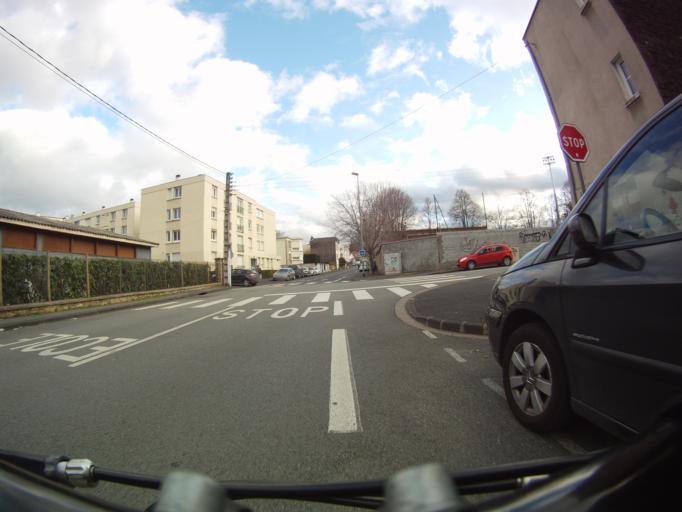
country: FR
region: Auvergne
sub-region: Departement du Puy-de-Dome
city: Beaumont
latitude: 45.7624
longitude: 3.0851
